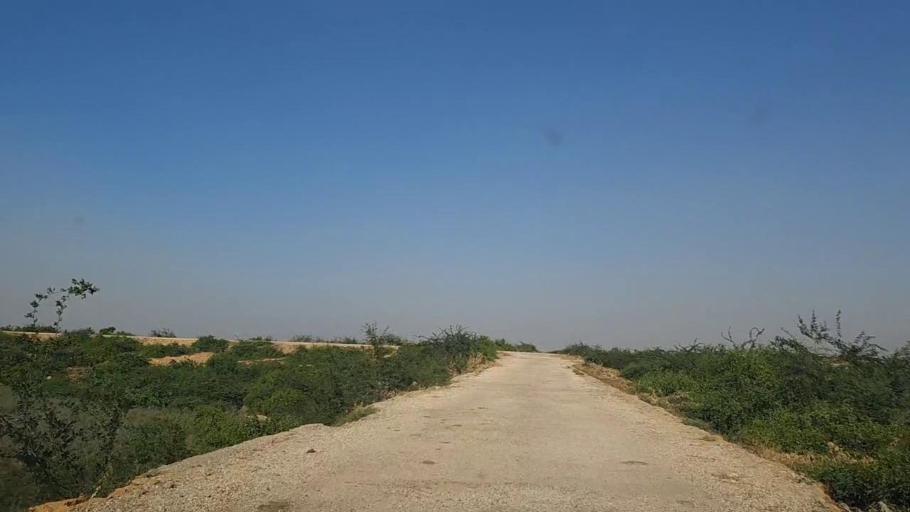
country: PK
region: Sindh
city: Daro Mehar
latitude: 25.0034
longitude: 68.1207
